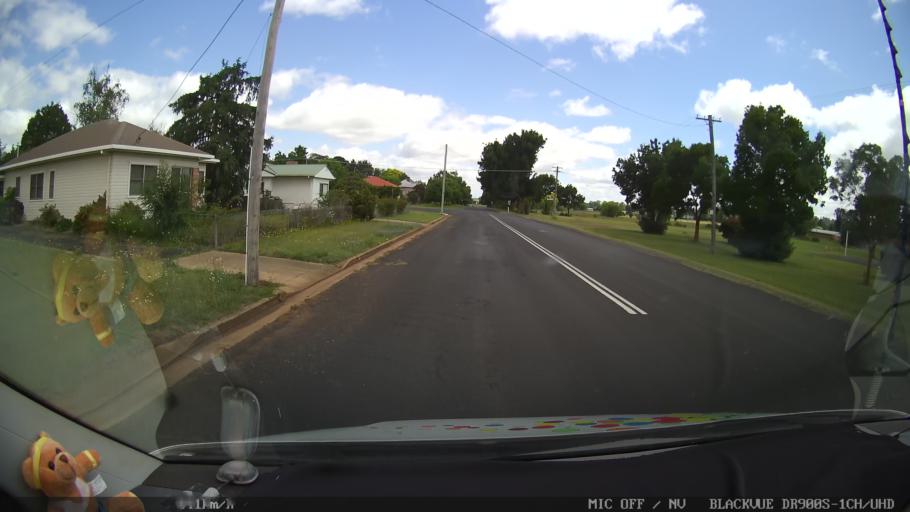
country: AU
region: New South Wales
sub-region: Glen Innes Severn
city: Glen Innes
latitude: -29.7315
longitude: 151.7335
